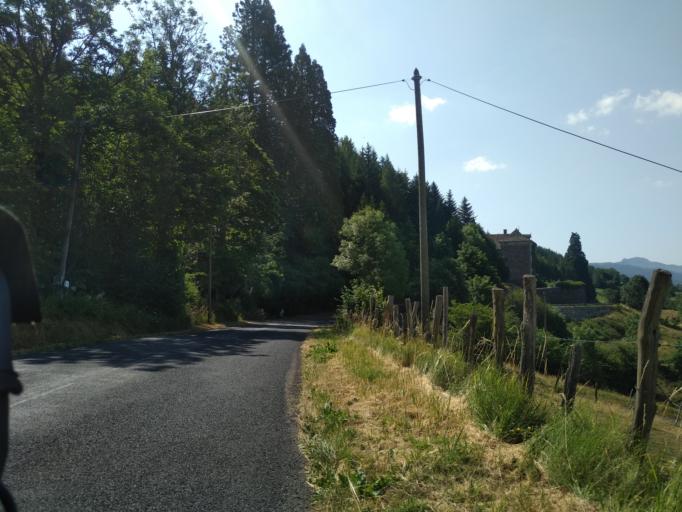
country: FR
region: Auvergne
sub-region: Departement du Cantal
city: Riom-es-Montagnes
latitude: 45.1998
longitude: 2.7171
